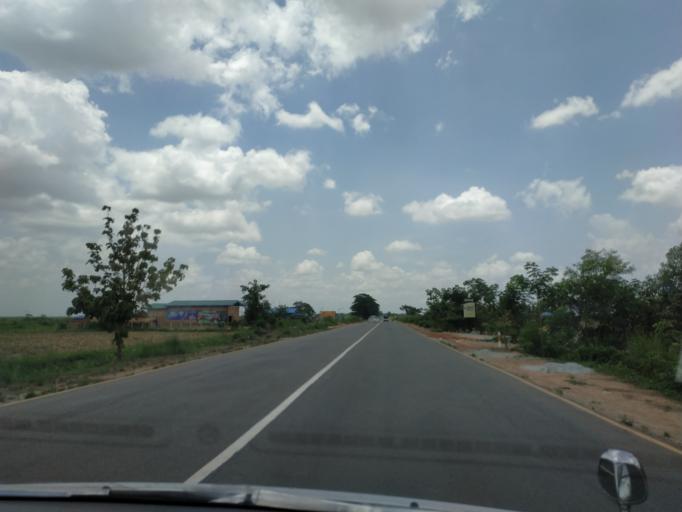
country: MM
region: Bago
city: Bago
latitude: 17.4702
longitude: 96.5574
